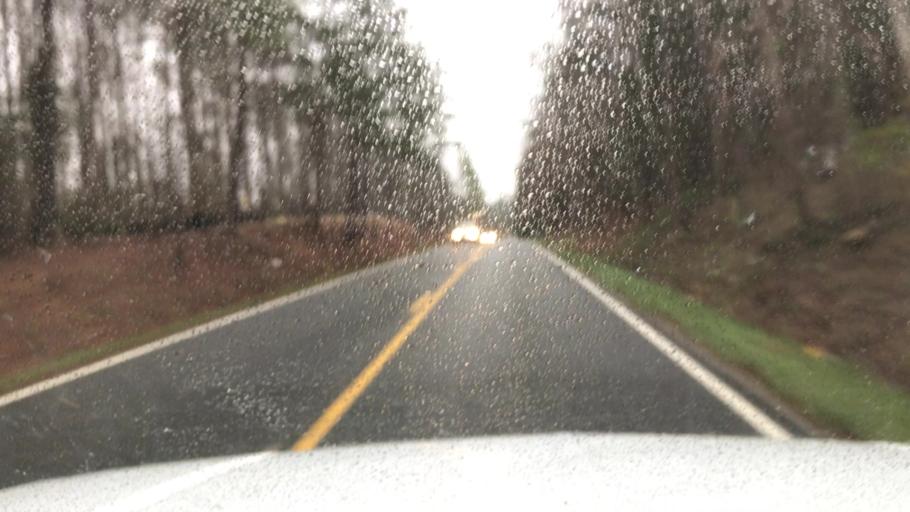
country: US
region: Virginia
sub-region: Henrico County
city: Short Pump
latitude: 37.6563
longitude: -77.6783
